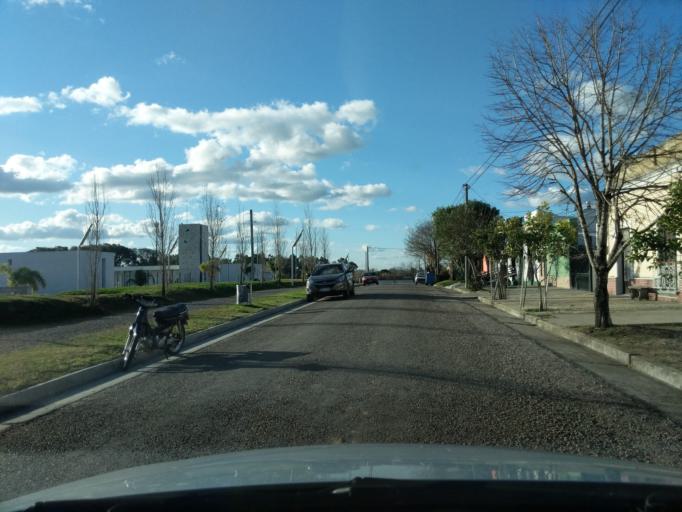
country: UY
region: Florida
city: Florida
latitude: -34.0995
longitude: -56.2316
